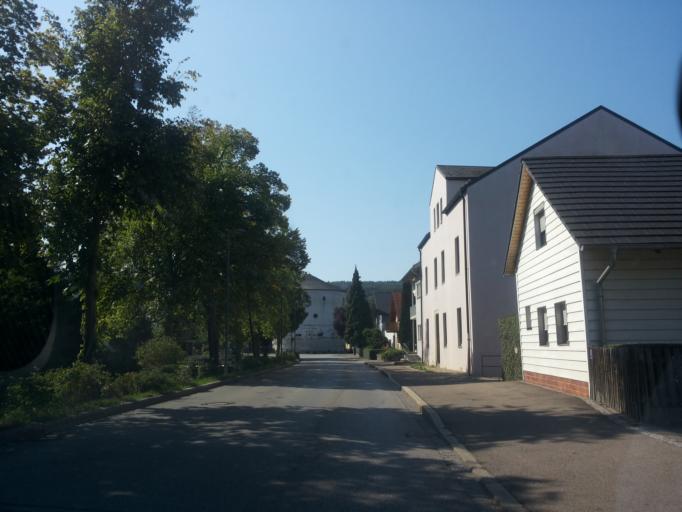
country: DE
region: Bavaria
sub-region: Lower Bavaria
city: Ihrlerstein
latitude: 48.9179
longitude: 11.8693
